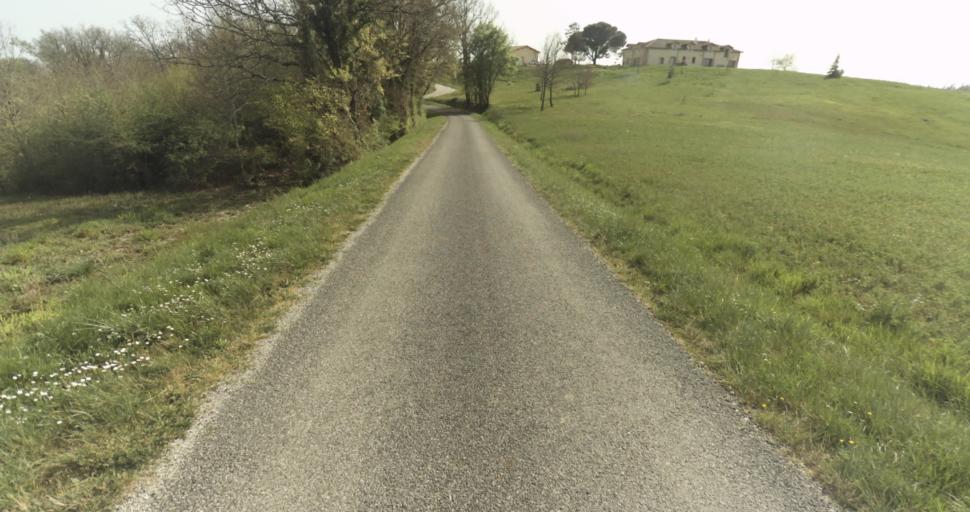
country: FR
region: Midi-Pyrenees
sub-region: Departement du Tarn-et-Garonne
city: Cazes-Mondenard
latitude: 44.1584
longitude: 1.1623
